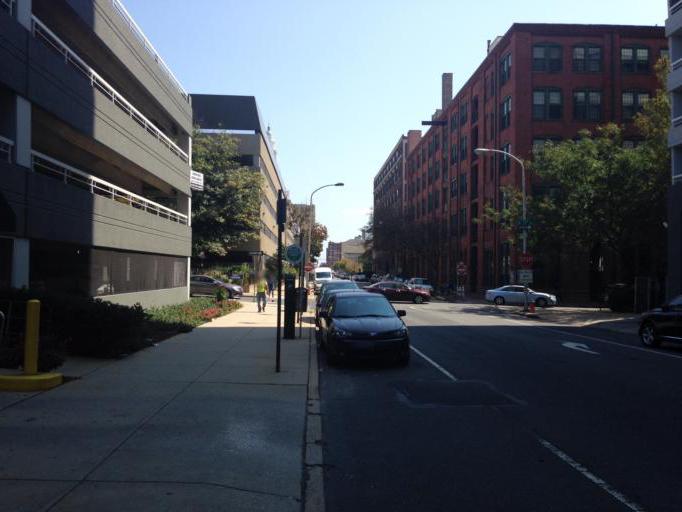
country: US
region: Pennsylvania
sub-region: Philadelphia County
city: Philadelphia
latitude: 39.9600
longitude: -75.1676
